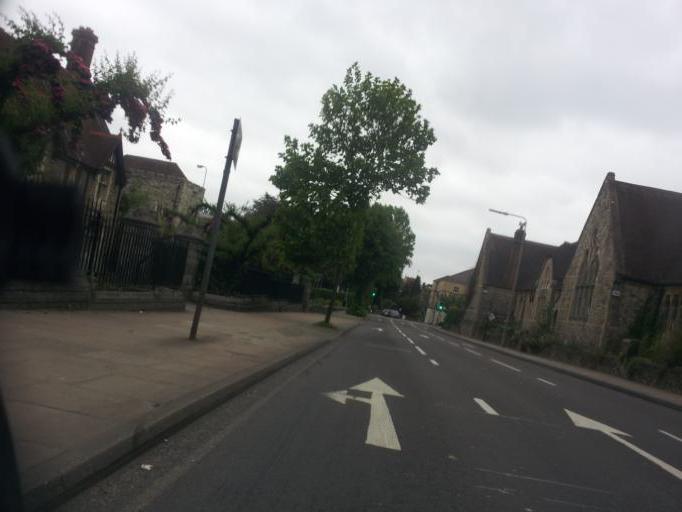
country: GB
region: England
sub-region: Kent
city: Maidstone
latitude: 51.2694
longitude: 0.5228
